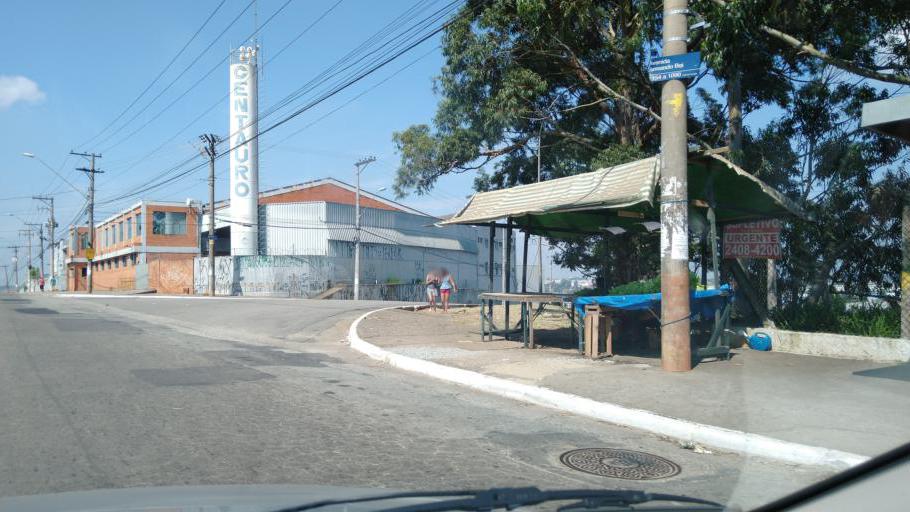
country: BR
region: Sao Paulo
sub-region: Aruja
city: Aruja
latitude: -23.4076
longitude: -46.3955
